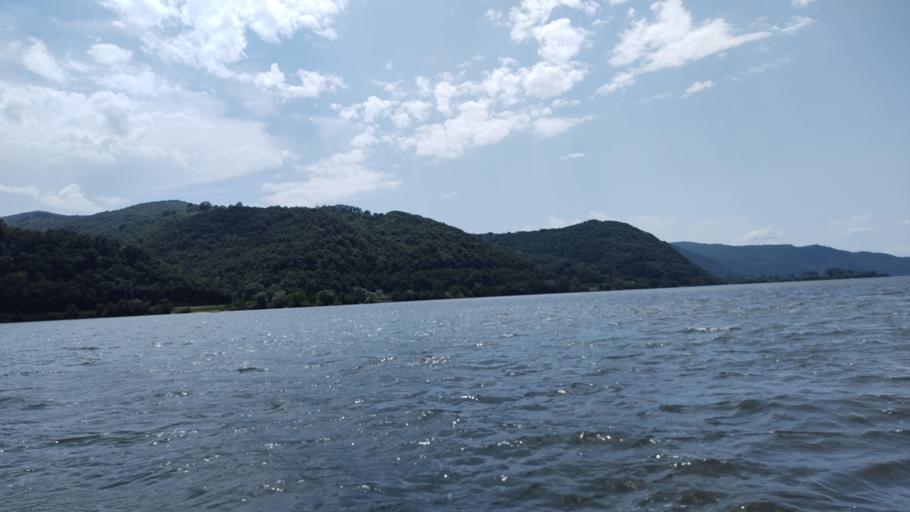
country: RO
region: Caras-Severin
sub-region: Comuna Berzasca
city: Liubcova
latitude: 44.6506
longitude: 21.8716
